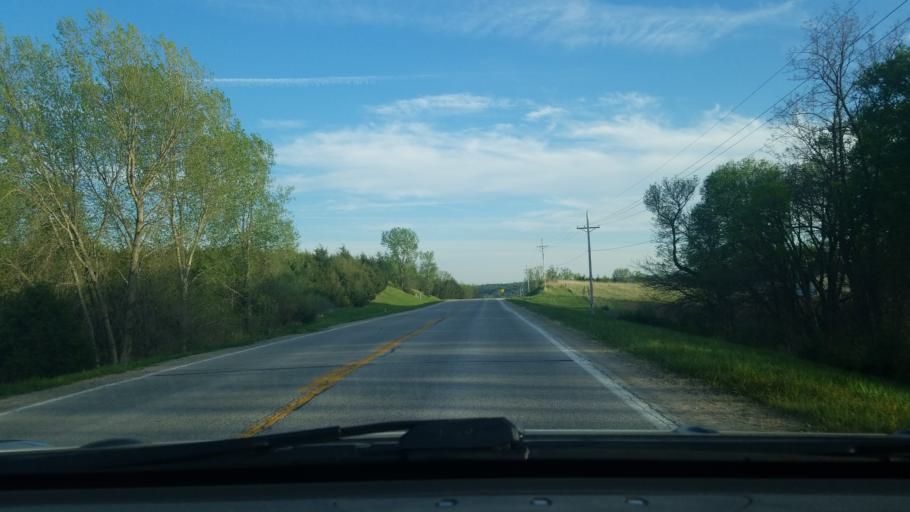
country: US
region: Nebraska
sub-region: Sarpy County
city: Offutt Air Force Base
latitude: 41.0771
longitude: -95.9664
